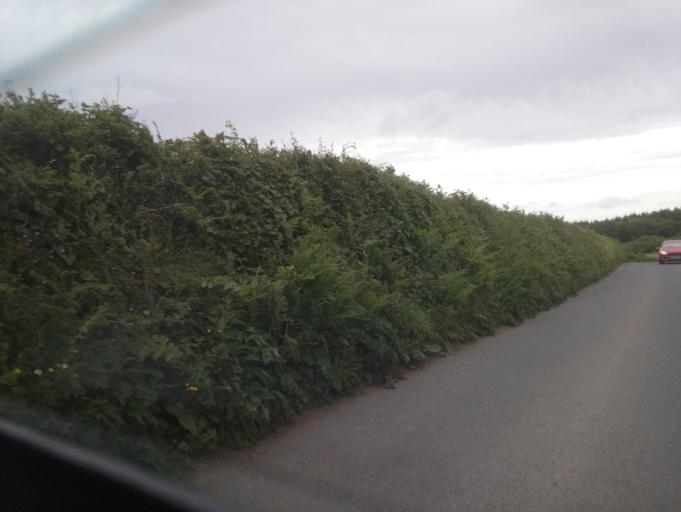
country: GB
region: England
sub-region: Devon
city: Dartmouth
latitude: 50.3360
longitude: -3.6496
